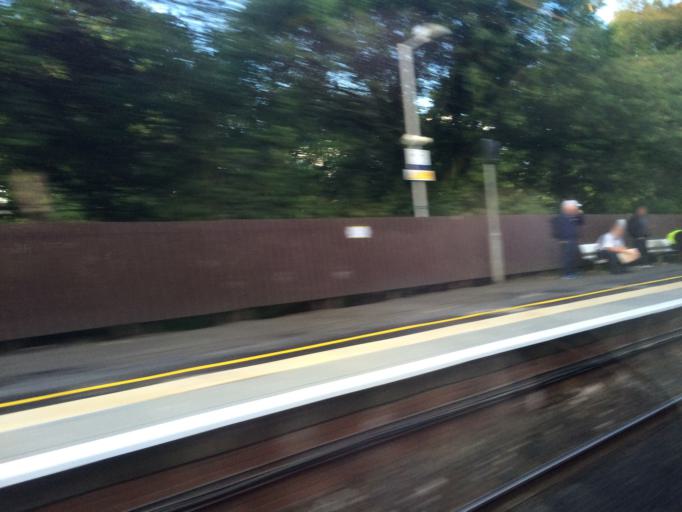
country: GB
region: Scotland
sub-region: East Dunbartonshire
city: Kirkintilloch
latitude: 55.9214
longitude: -4.1536
